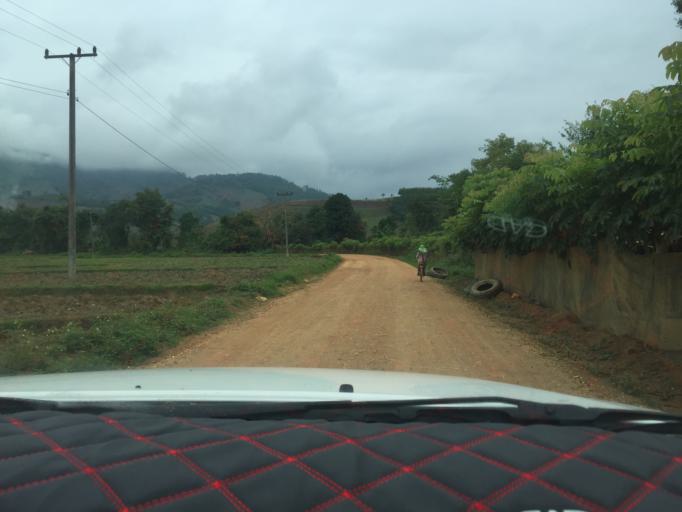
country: TH
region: Phayao
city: Phu Sang
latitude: 19.6779
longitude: 100.5090
